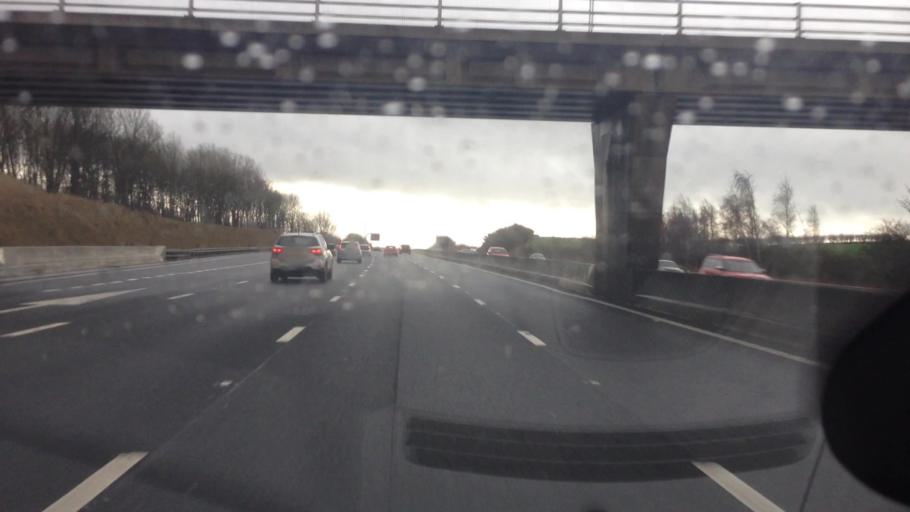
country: GB
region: England
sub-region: City and Borough of Wakefield
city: Ossett
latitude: 53.6900
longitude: -1.5566
